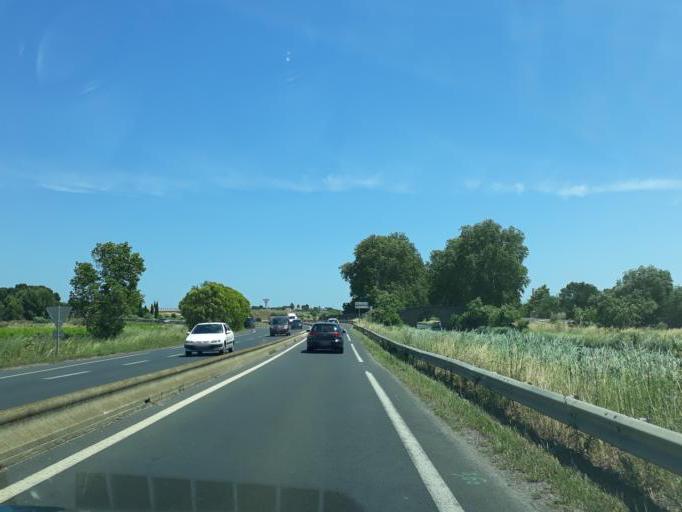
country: FR
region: Languedoc-Roussillon
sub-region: Departement de l'Herault
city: Cers
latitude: 43.3157
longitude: 3.3113
